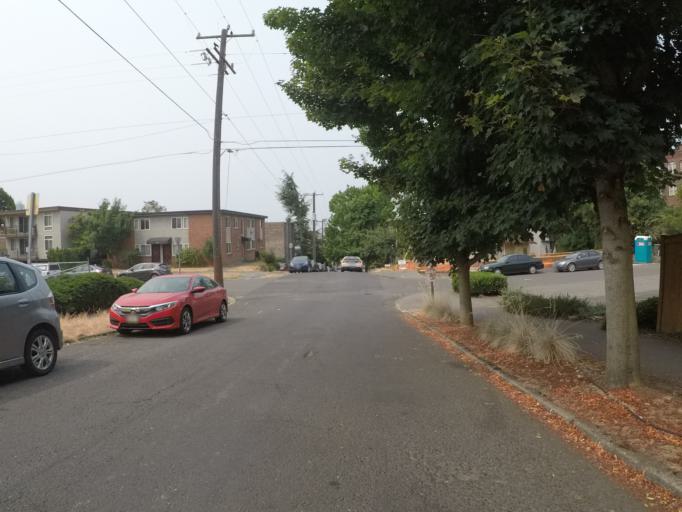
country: US
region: Washington
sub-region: King County
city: Seattle
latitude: 47.6219
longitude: -122.3153
